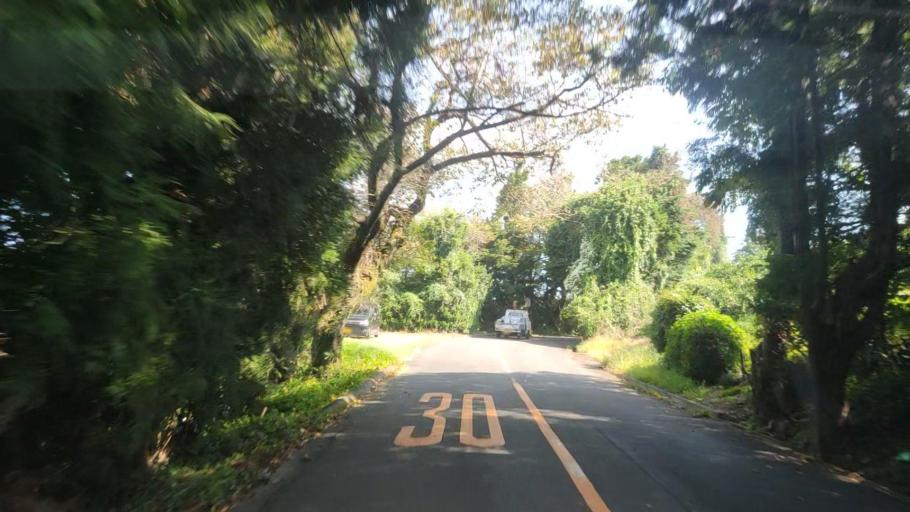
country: JP
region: Shizuoka
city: Shizuoka-shi
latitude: 34.9811
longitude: 138.4767
